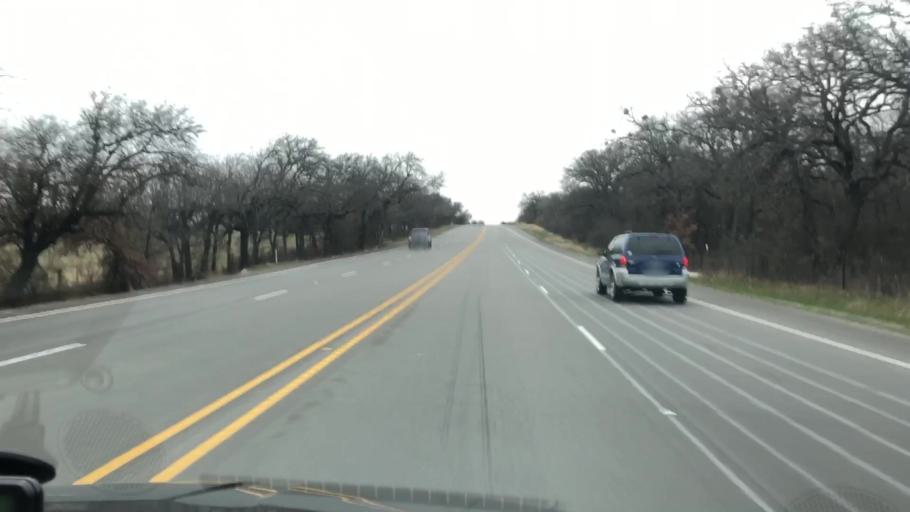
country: US
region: Texas
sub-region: Hamilton County
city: Hico
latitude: 32.0114
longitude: -98.0622
